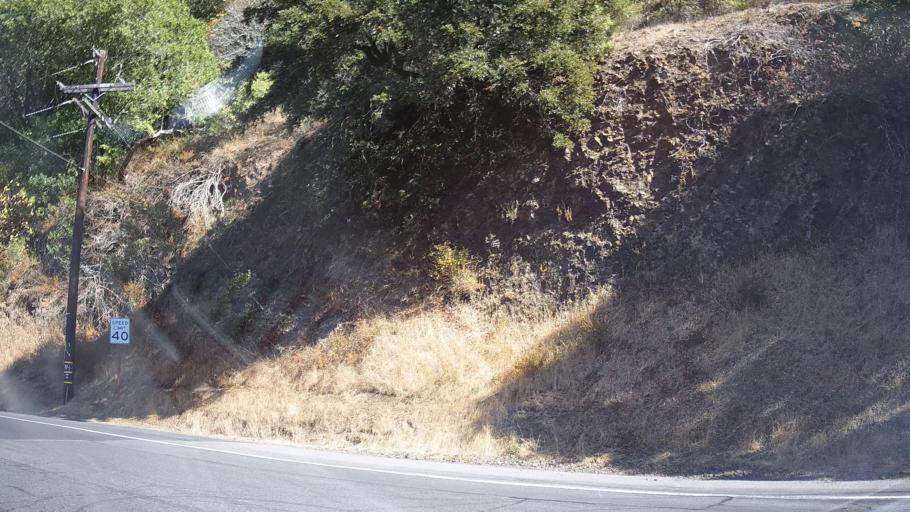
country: US
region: California
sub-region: Marin County
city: Lagunitas-Forest Knolls
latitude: 38.0691
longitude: -122.7637
